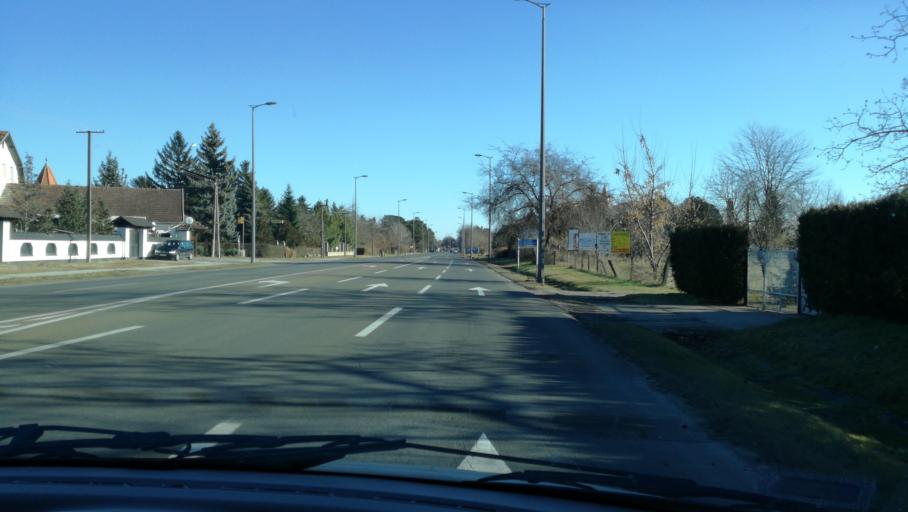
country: RS
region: Autonomna Pokrajina Vojvodina
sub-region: Severnobacki Okrug
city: Subotica
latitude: 46.1034
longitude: 19.7469
